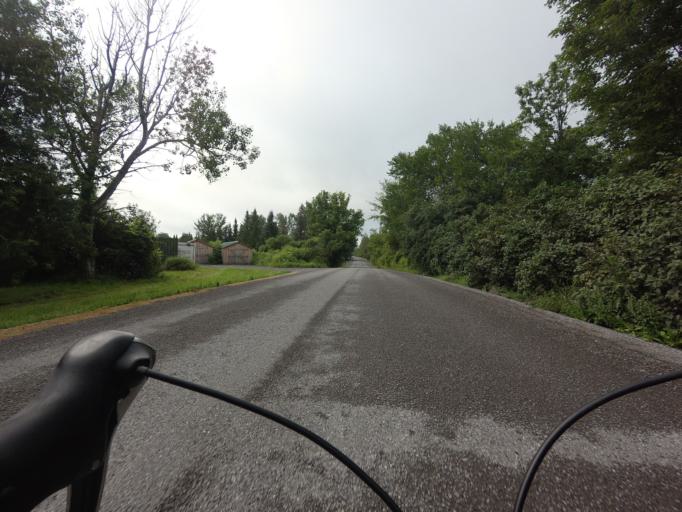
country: CA
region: Ontario
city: Bells Corners
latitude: 45.0823
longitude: -75.7573
